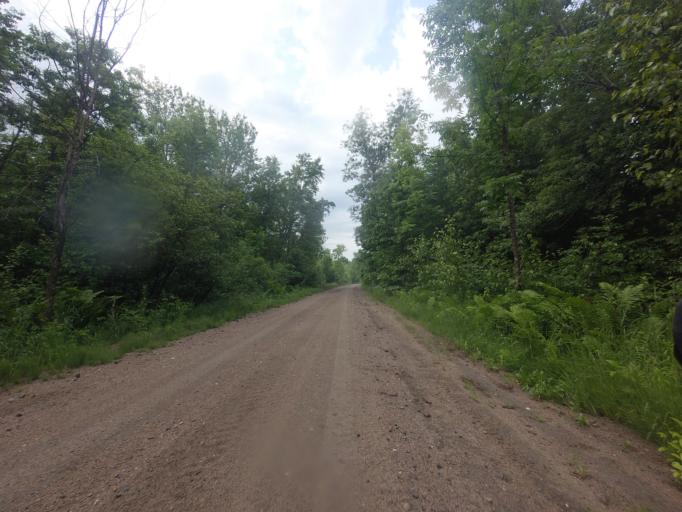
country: CA
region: Quebec
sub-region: Outaouais
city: Maniwaki
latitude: 46.3268
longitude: -76.0046
